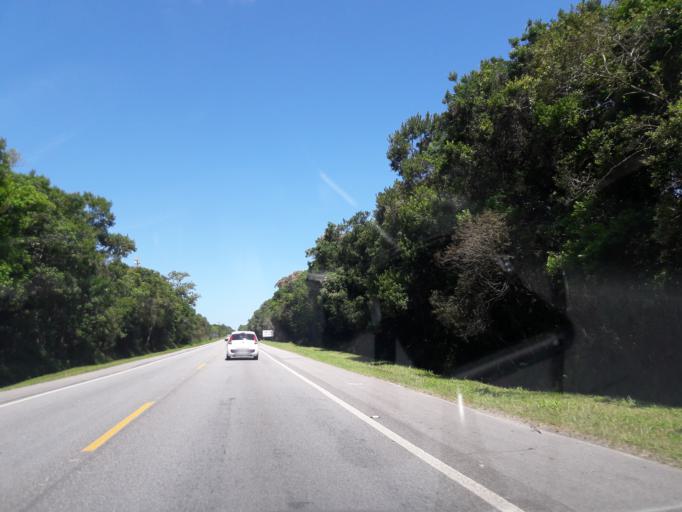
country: BR
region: Parana
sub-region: Pontal Do Parana
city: Pontal do Parana
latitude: -25.6111
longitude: -48.5515
